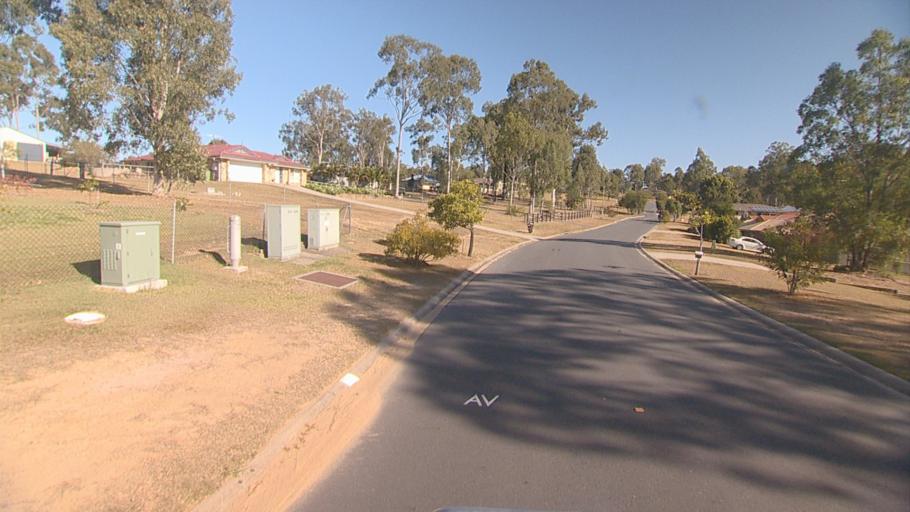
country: AU
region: Queensland
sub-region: Logan
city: Cedar Vale
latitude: -27.8635
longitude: 153.0376
